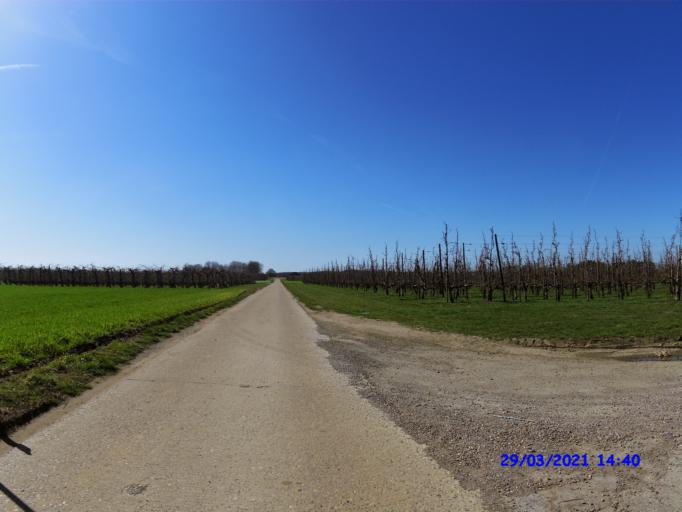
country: BE
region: Flanders
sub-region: Provincie Vlaams-Brabant
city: Lubbeek
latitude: 50.9192
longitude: 4.8873
